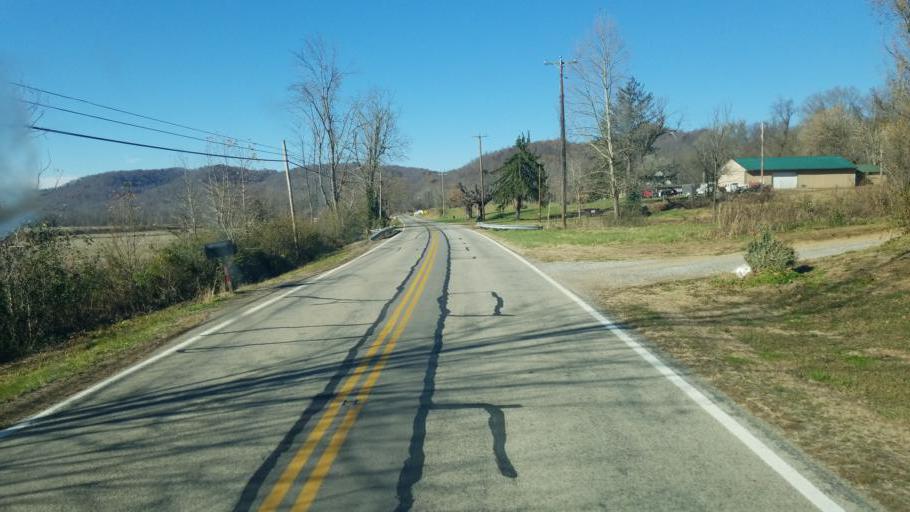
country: US
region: Kentucky
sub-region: Lewis County
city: Vanceburg
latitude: 38.6340
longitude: -83.2150
